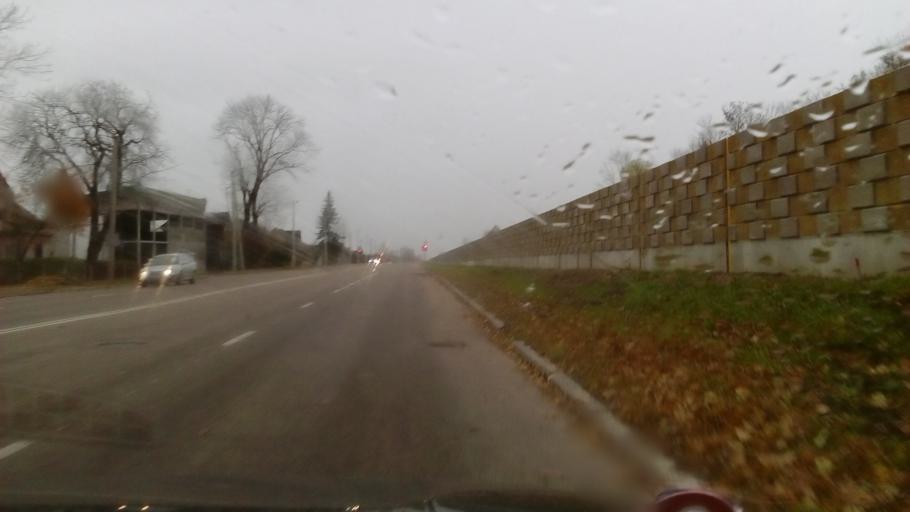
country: LT
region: Marijampoles apskritis
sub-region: Marijampole Municipality
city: Marijampole
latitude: 54.5456
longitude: 23.3565
